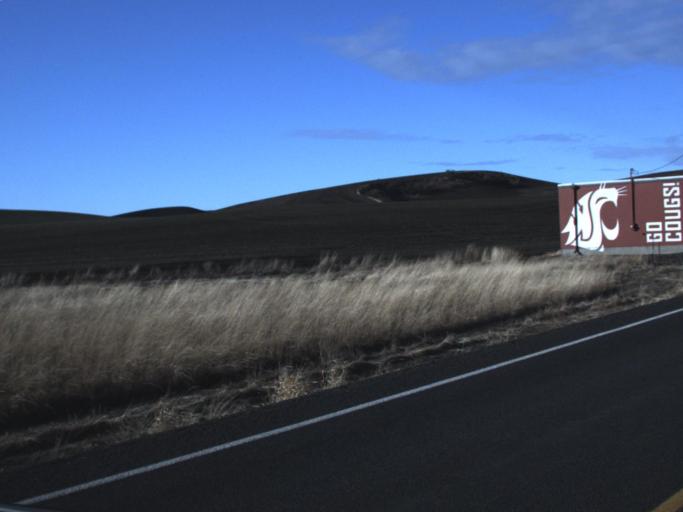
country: US
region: Washington
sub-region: Whitman County
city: Pullman
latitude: 46.7249
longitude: -117.2359
